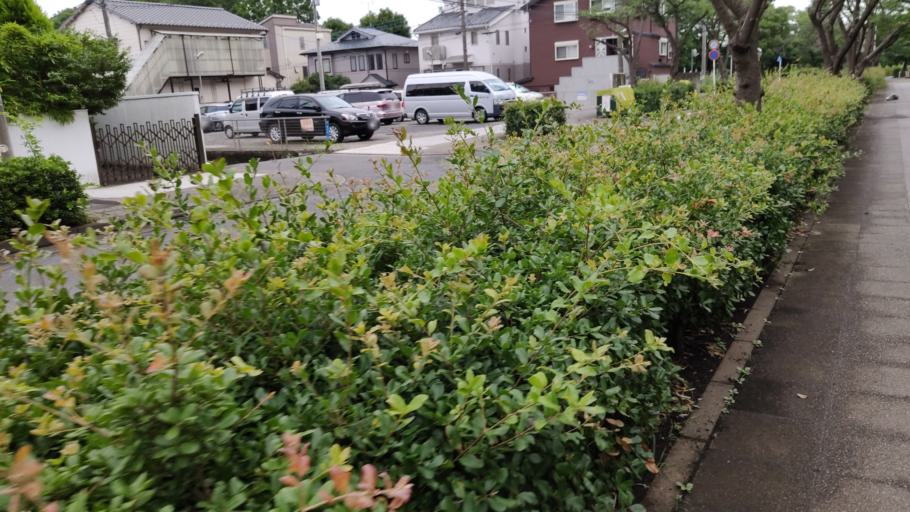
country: JP
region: Kanagawa
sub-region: Kawasaki-shi
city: Kawasaki
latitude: 35.5891
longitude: 139.6504
